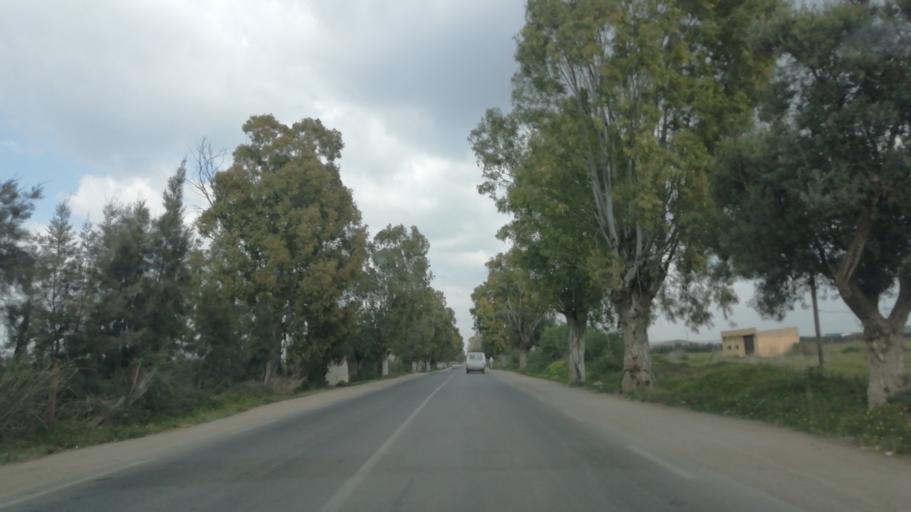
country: DZ
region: Mascara
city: Mascara
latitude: 35.6291
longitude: 0.1283
